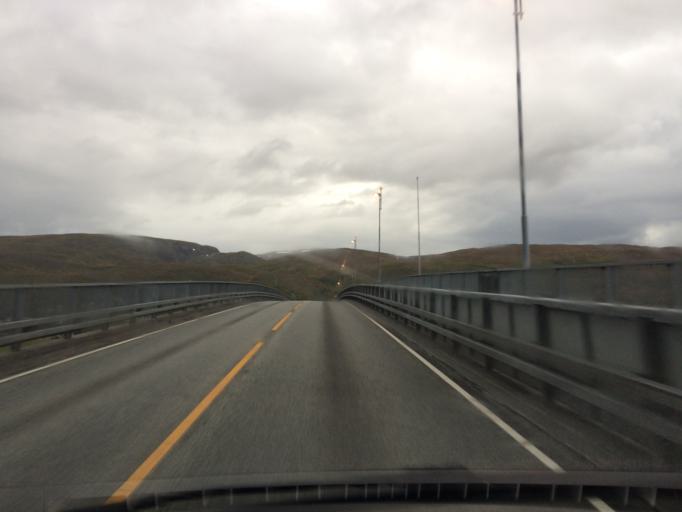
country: NO
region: Troms
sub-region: Tromso
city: Tromso
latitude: 69.6907
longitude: 18.9033
